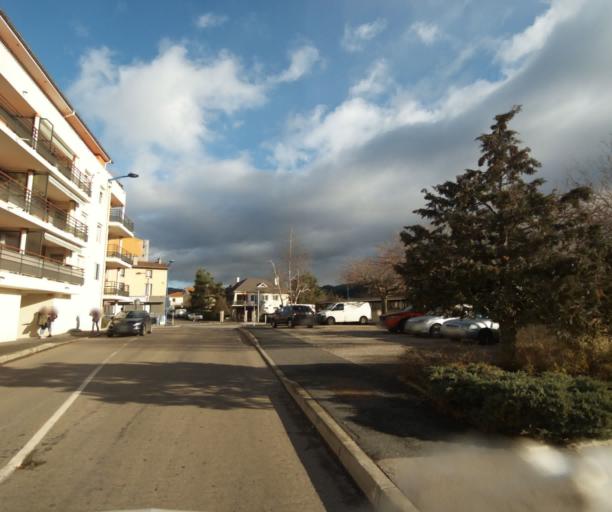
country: FR
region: Rhone-Alpes
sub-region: Departement de la Loire
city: La Talaudiere
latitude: 45.4819
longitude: 4.4382
